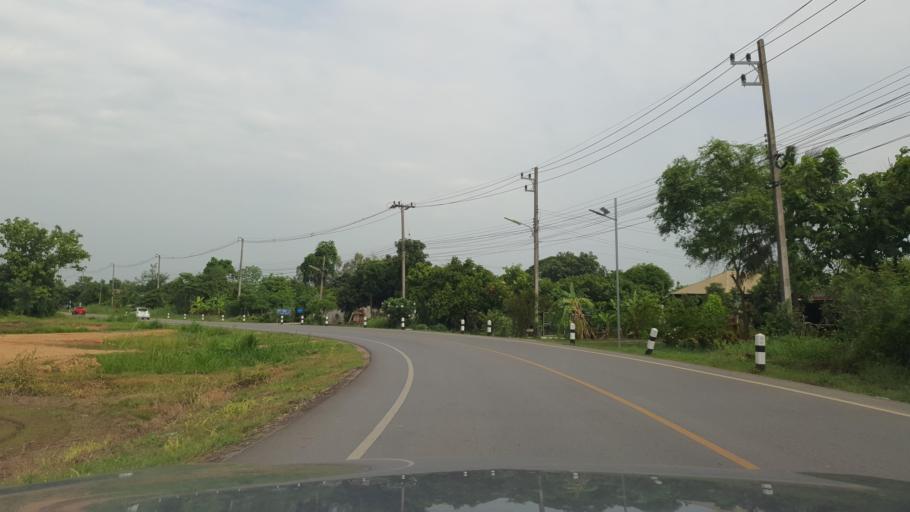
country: TH
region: Phitsanulok
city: Phitsanulok
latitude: 16.8157
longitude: 100.2002
